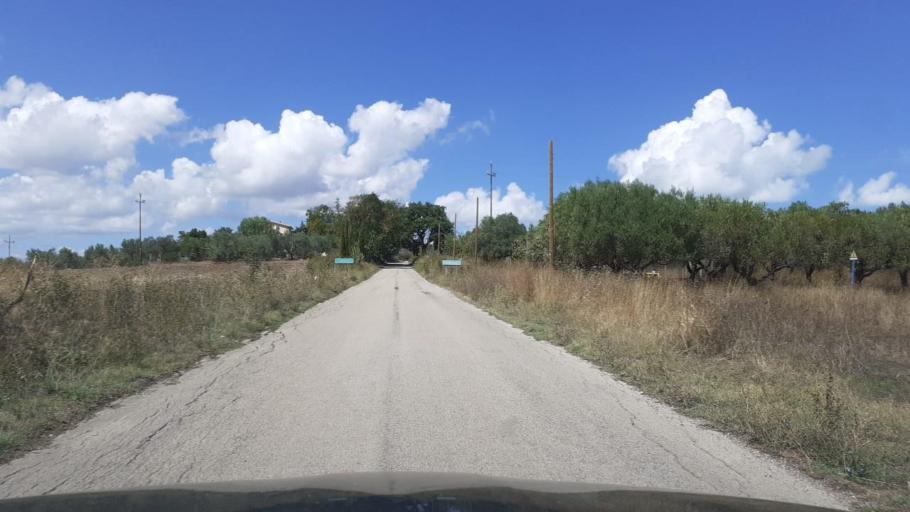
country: IT
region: Molise
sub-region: Provincia di Campobasso
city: San Giacomo degli Schiavoni
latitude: 41.9862
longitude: 14.9168
